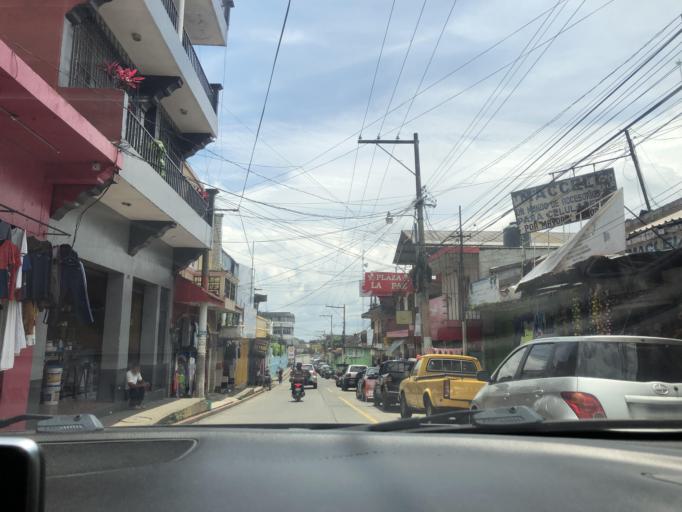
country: GT
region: Quetzaltenango
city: Coatepeque
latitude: 14.7032
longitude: -91.8635
